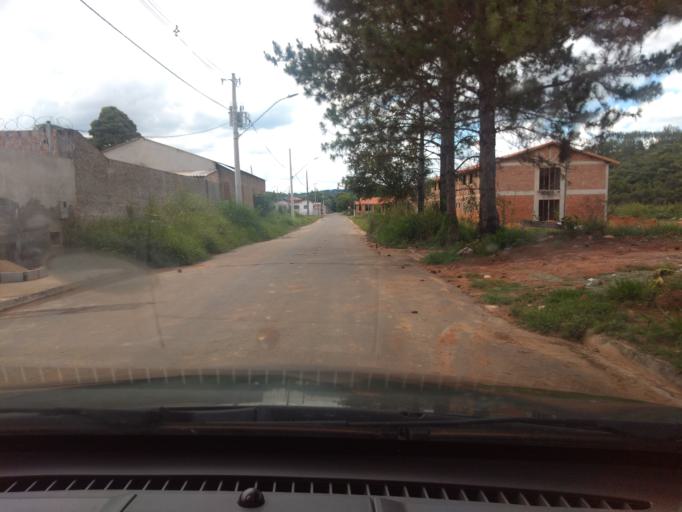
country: BR
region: Minas Gerais
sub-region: Tres Coracoes
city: Tres Coracoes
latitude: -21.6726
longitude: -45.2649
